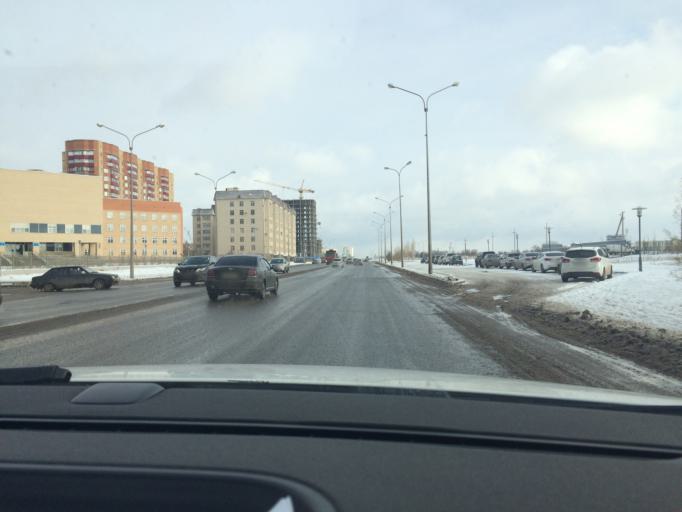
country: KZ
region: Astana Qalasy
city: Astana
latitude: 51.1228
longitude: 71.4811
